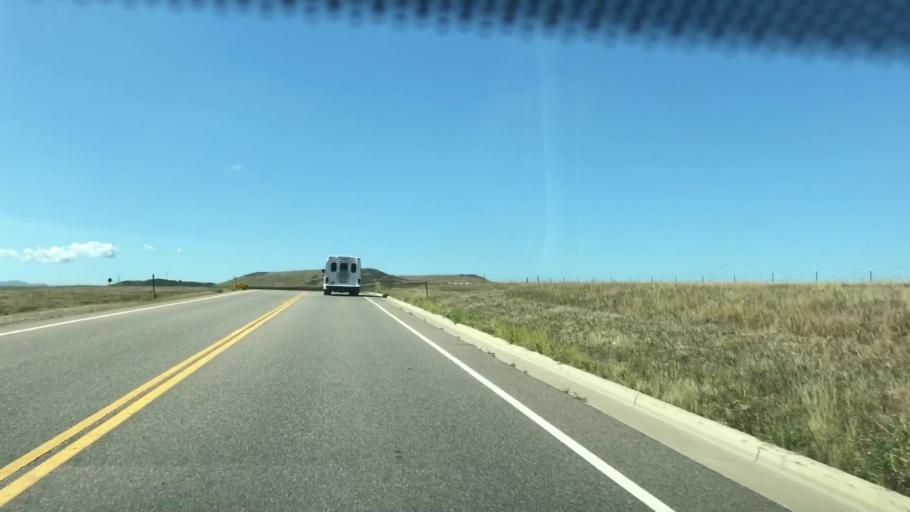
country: US
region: Colorado
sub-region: Douglas County
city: Meridian
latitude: 39.5270
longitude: -104.8540
